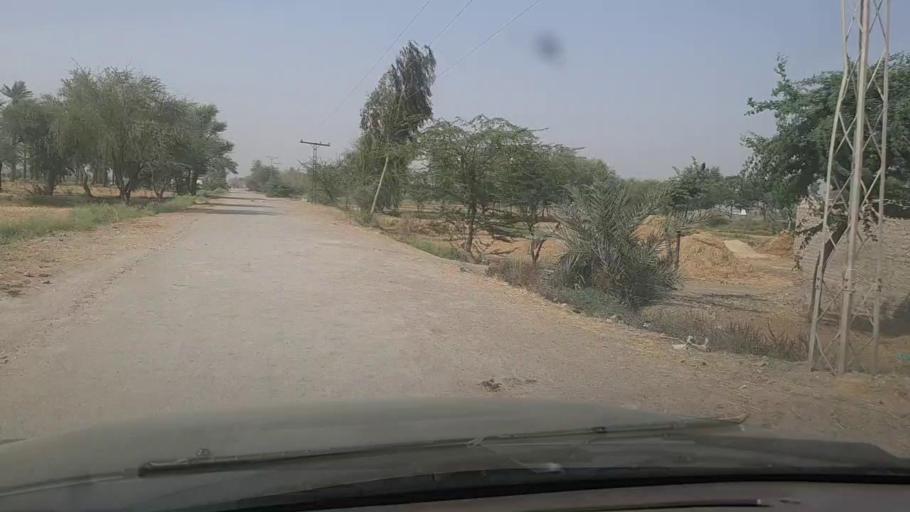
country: PK
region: Sindh
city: Garhi Yasin
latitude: 27.8726
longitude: 68.5597
